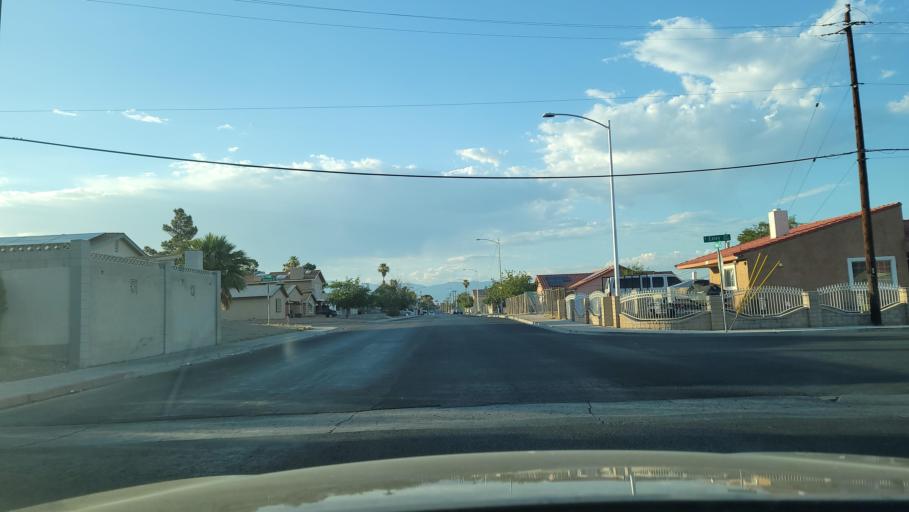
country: US
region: Nevada
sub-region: Clark County
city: Winchester
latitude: 36.1461
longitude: -115.1232
